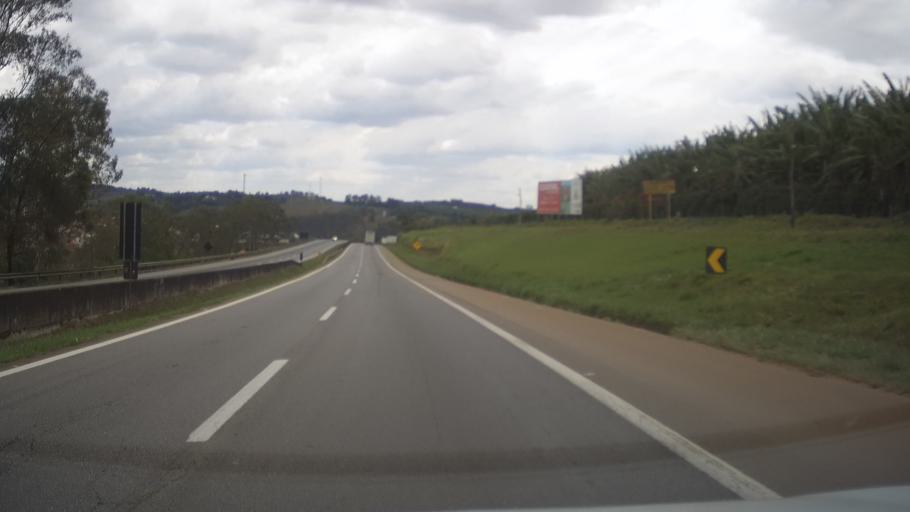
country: BR
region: Minas Gerais
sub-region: Nepomuceno
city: Nepomuceno
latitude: -21.4605
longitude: -45.2074
